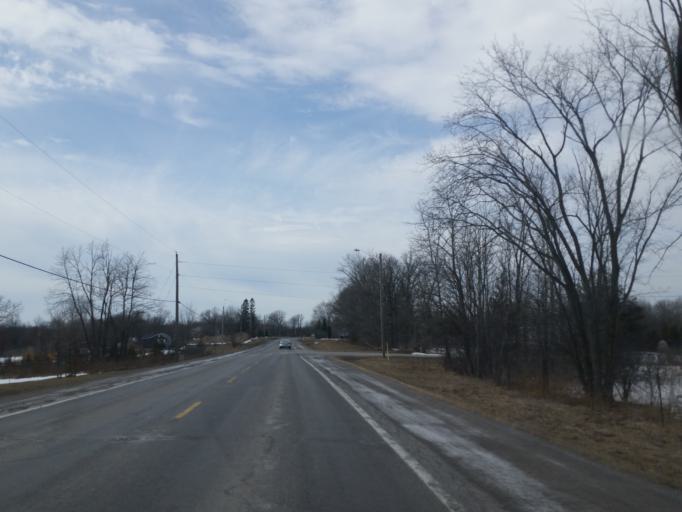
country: CA
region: Ontario
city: Deseronto
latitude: 44.1923
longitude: -77.2007
